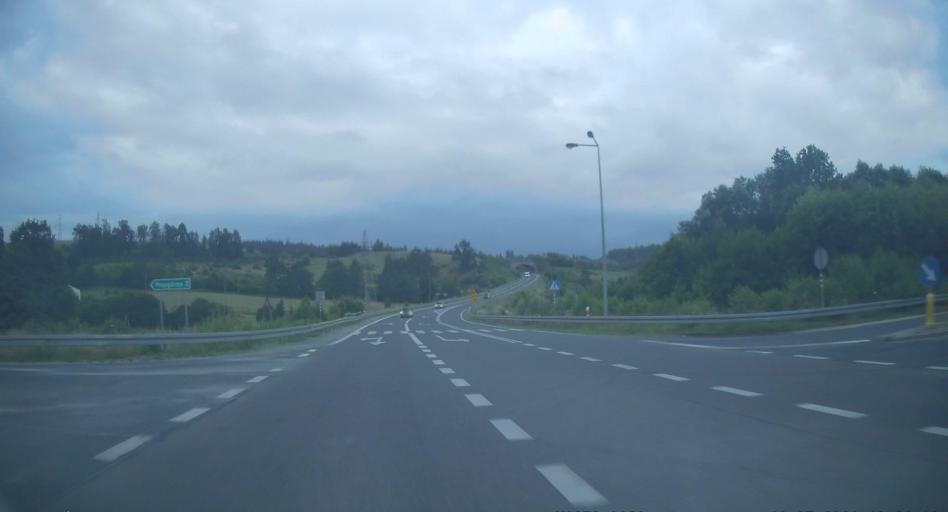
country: PL
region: Lower Silesian Voivodeship
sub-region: Powiat klodzki
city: Nowa Ruda
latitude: 50.5967
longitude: 16.5186
